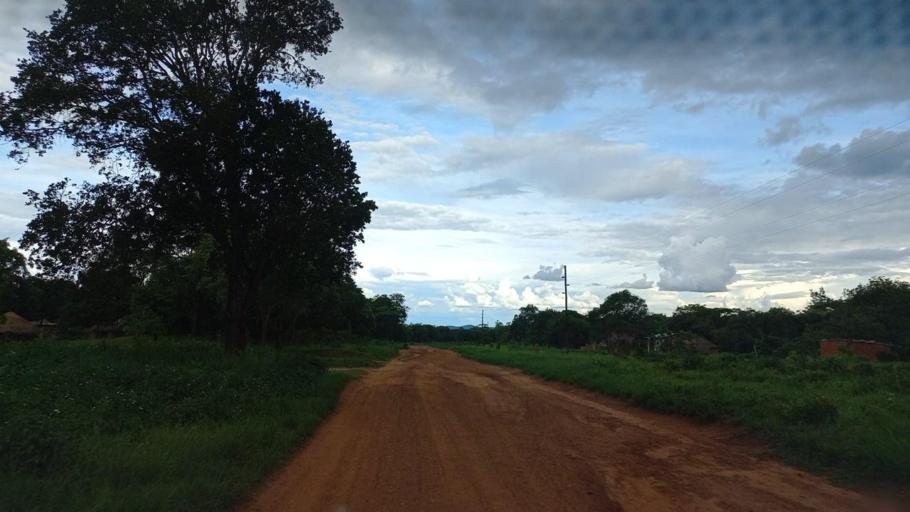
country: ZM
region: North-Western
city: Mwinilunga
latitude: -11.7745
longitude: 24.3910
